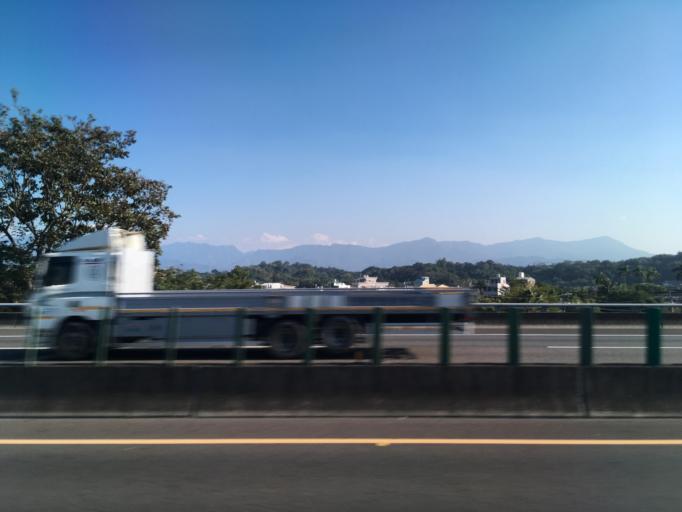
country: TW
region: Taiwan
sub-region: Chiayi
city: Jiayi Shi
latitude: 23.4348
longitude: 120.4750
